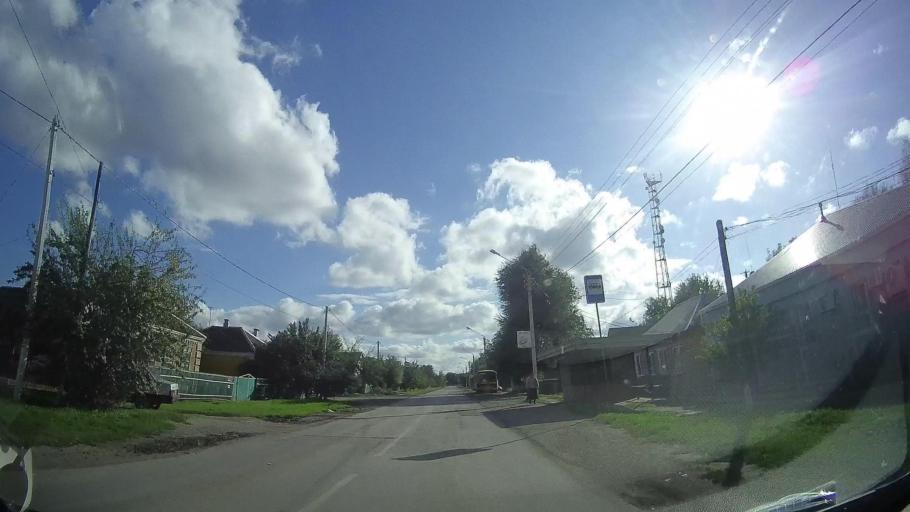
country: RU
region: Rostov
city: Tselina
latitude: 46.5339
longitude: 41.0337
